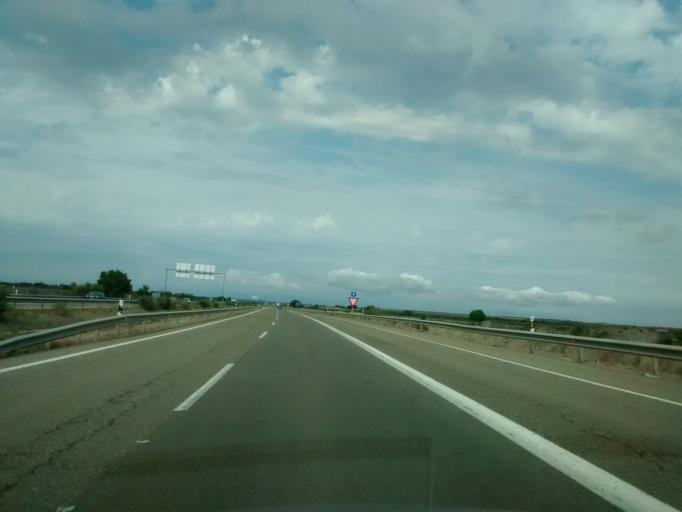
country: ES
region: Aragon
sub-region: Provincia de Zaragoza
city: Zuera
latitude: 41.9140
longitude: -0.7541
